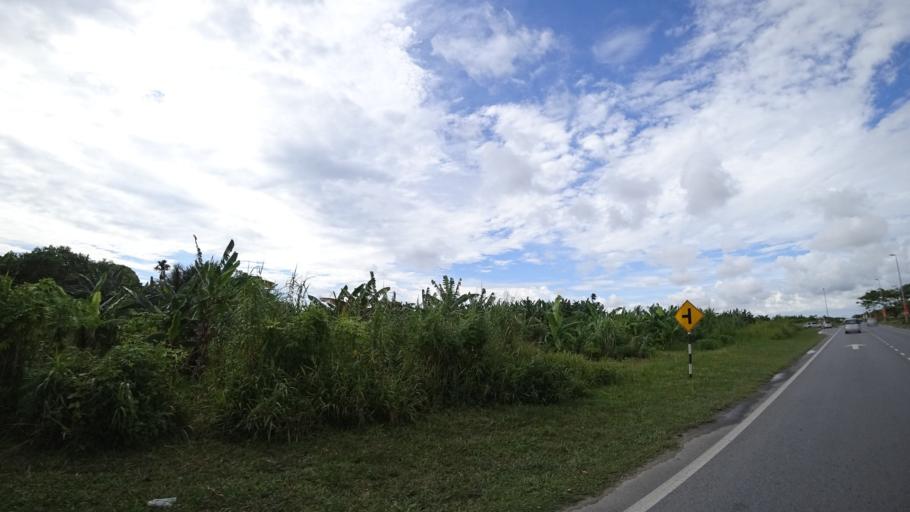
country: MY
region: Sarawak
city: Miri
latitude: 4.4655
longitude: 114.0419
